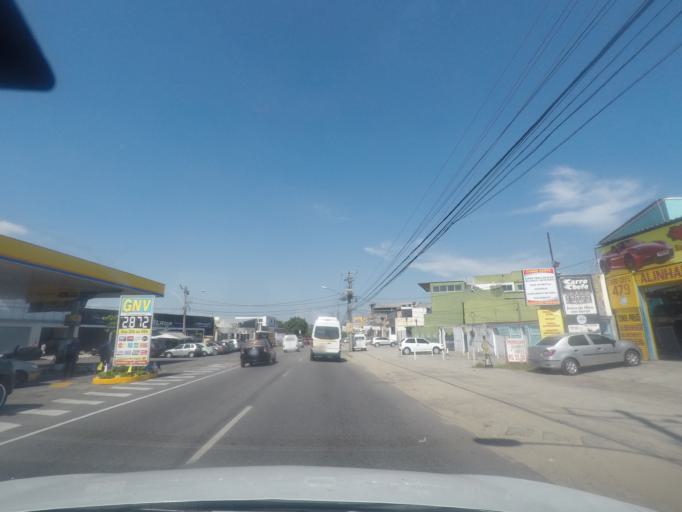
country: BR
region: Rio de Janeiro
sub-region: Nilopolis
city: Nilopolis
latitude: -22.8789
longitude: -43.4501
